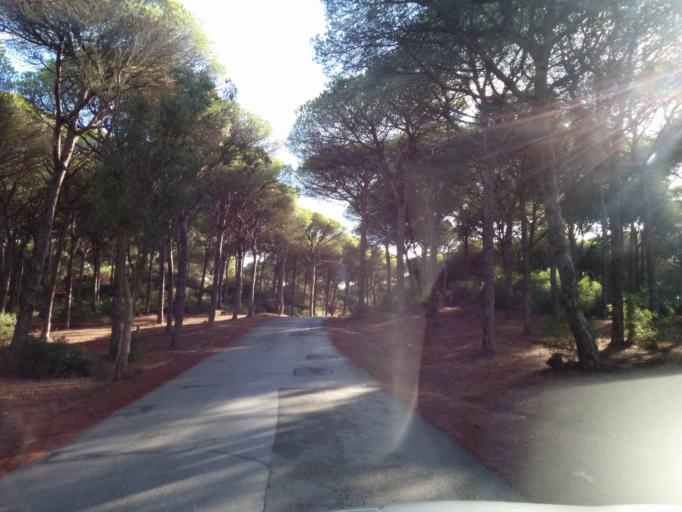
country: ES
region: Andalusia
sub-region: Provincia de Cadiz
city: Vejer de la Frontera
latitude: 36.2002
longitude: -5.9806
